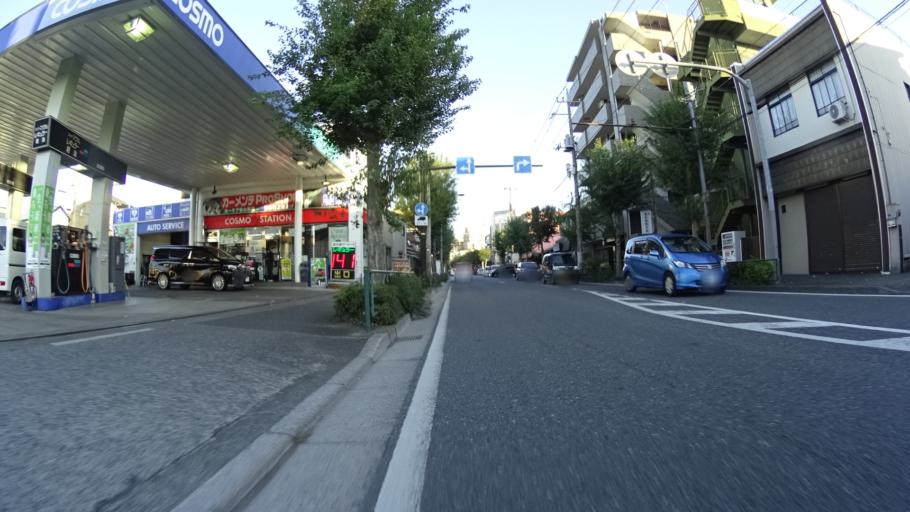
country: JP
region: Tokyo
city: Hachioji
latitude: 35.6618
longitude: 139.3130
